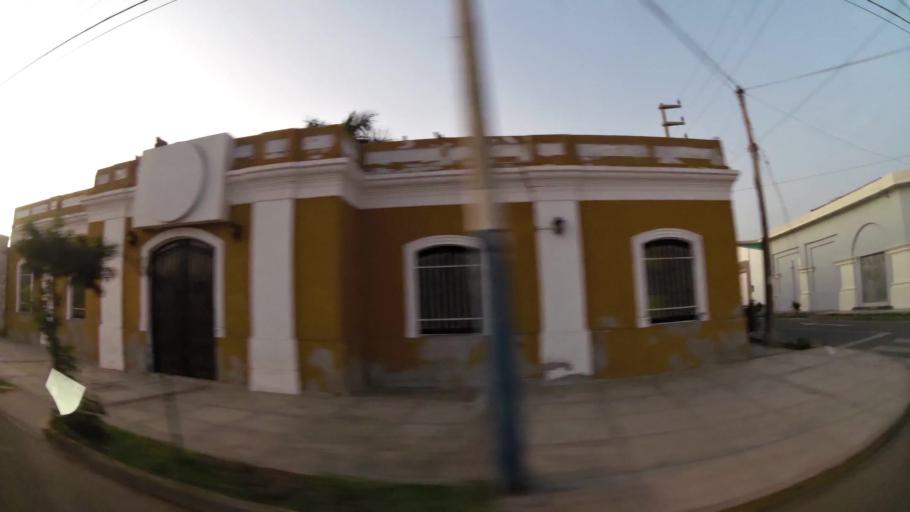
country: PE
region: Ica
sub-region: Provincia de Pisco
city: Pisco
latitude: -13.7094
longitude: -76.2171
